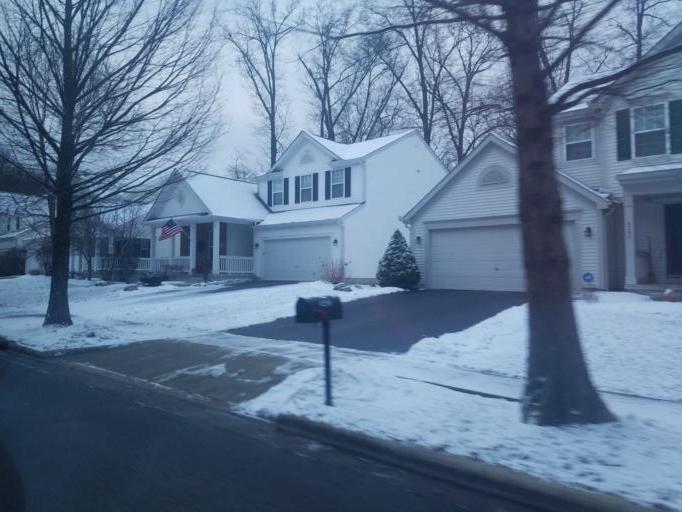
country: US
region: Ohio
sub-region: Franklin County
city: New Albany
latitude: 40.0679
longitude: -82.8494
